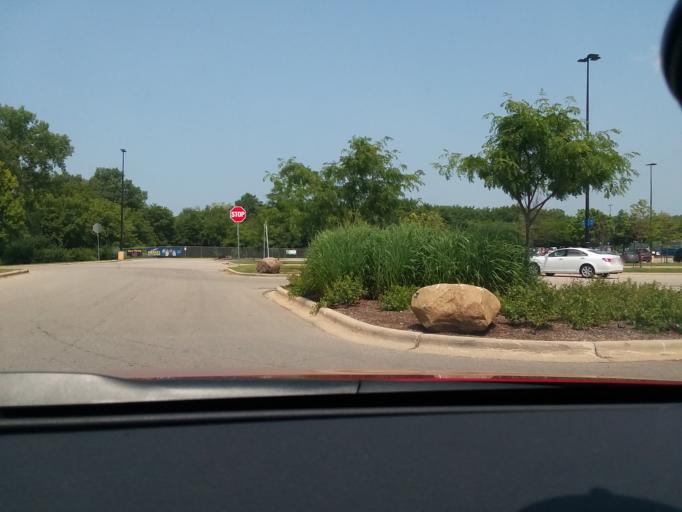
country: US
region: Wisconsin
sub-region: Dane County
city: Monona
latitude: 43.1096
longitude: -89.3141
